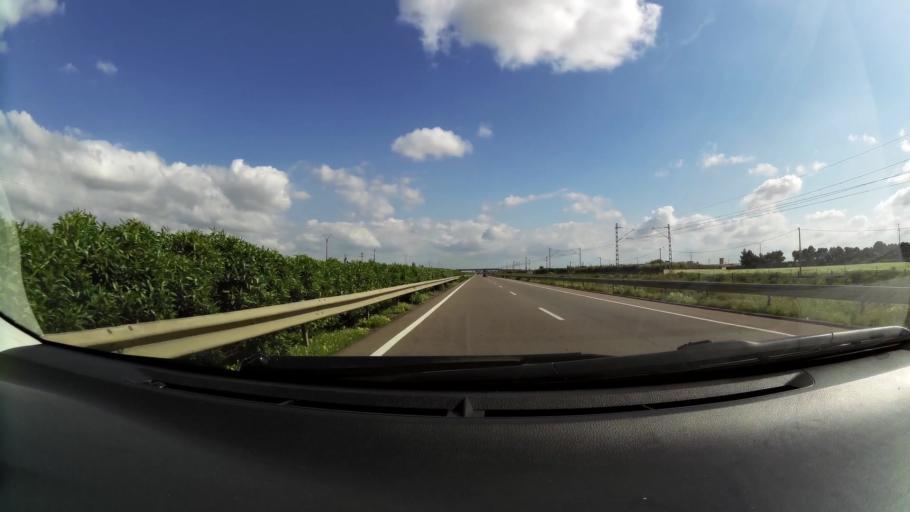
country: MA
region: Chaouia-Ouardigha
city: Nouaseur
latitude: 33.3401
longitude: -7.6120
